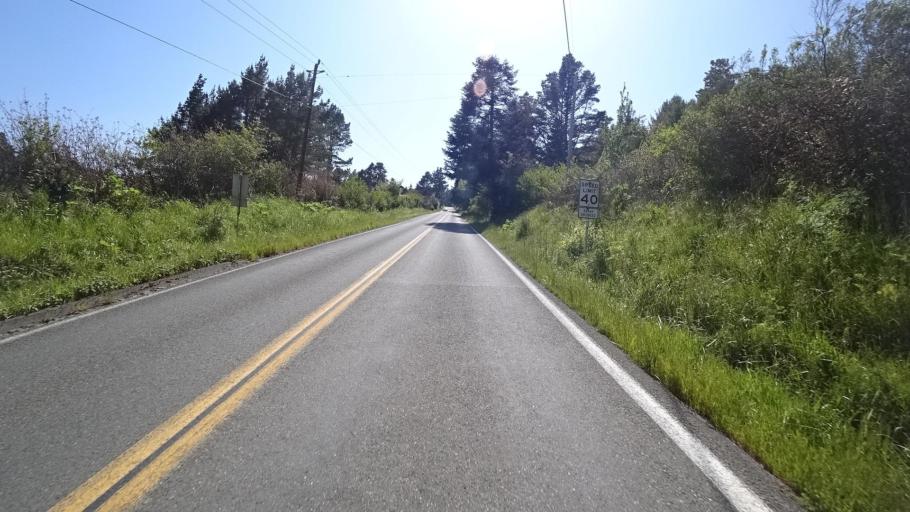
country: US
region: California
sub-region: Humboldt County
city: Hydesville
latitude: 40.5566
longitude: -124.1068
